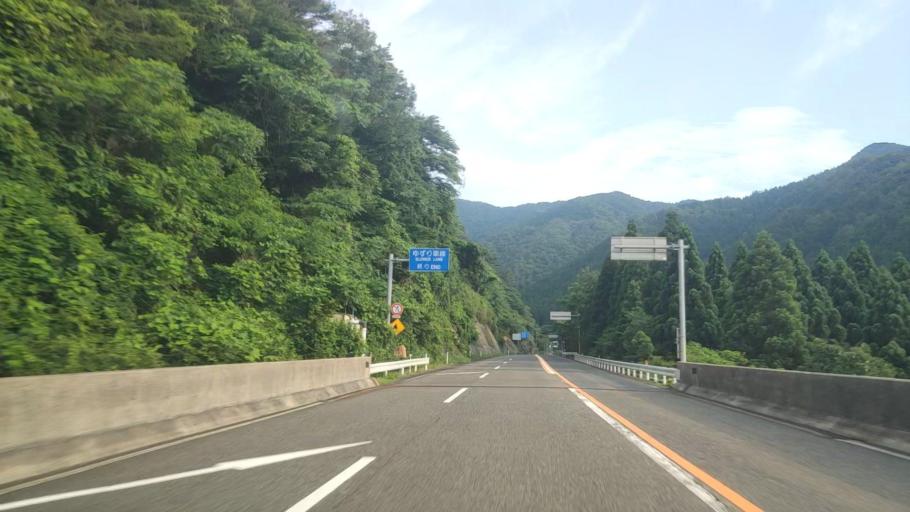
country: JP
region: Tottori
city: Kurayoshi
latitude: 35.3216
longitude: 133.7564
